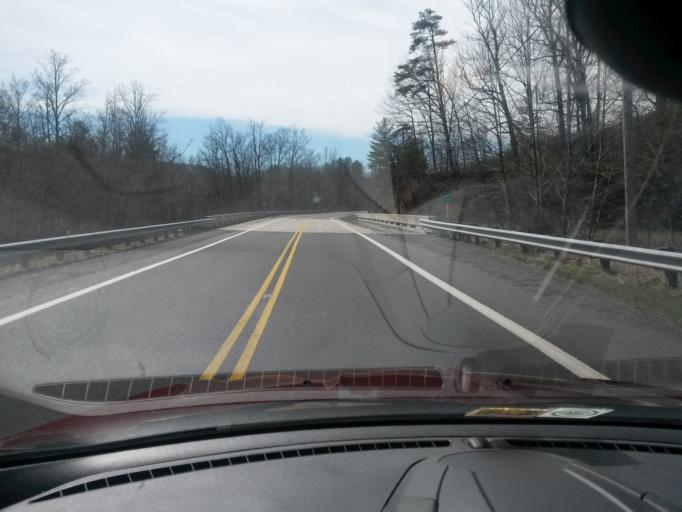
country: US
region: West Virginia
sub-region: Greenbrier County
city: White Sulphur Springs
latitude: 37.6894
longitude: -80.2231
